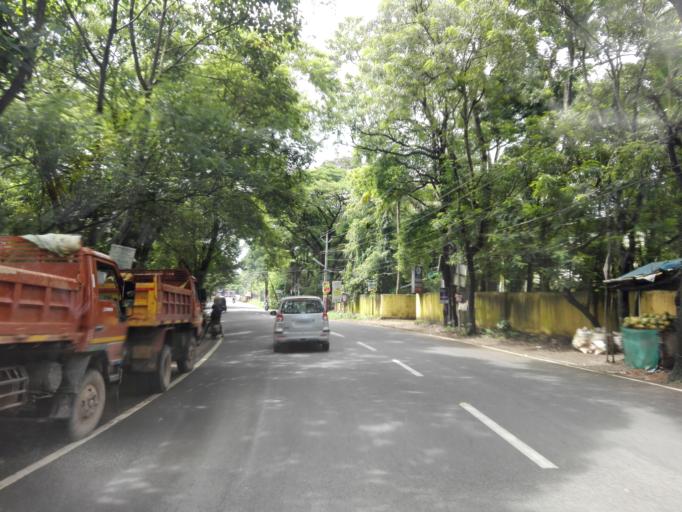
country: IN
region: Kerala
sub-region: Ernakulam
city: Elur
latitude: 10.0200
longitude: 76.3348
